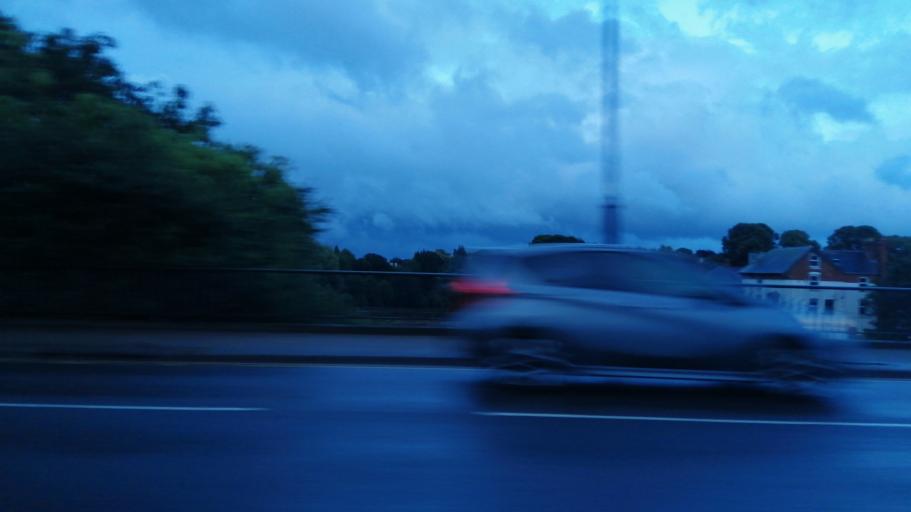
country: GB
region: England
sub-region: Herefordshire
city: Hereford
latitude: 52.0524
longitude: -2.7199
